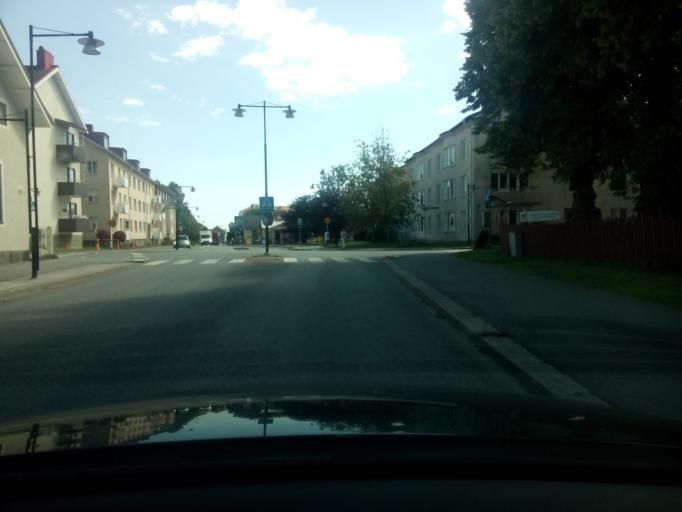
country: SE
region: Soedermanland
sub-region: Nykopings Kommun
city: Nykoping
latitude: 58.7510
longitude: 17.0128
